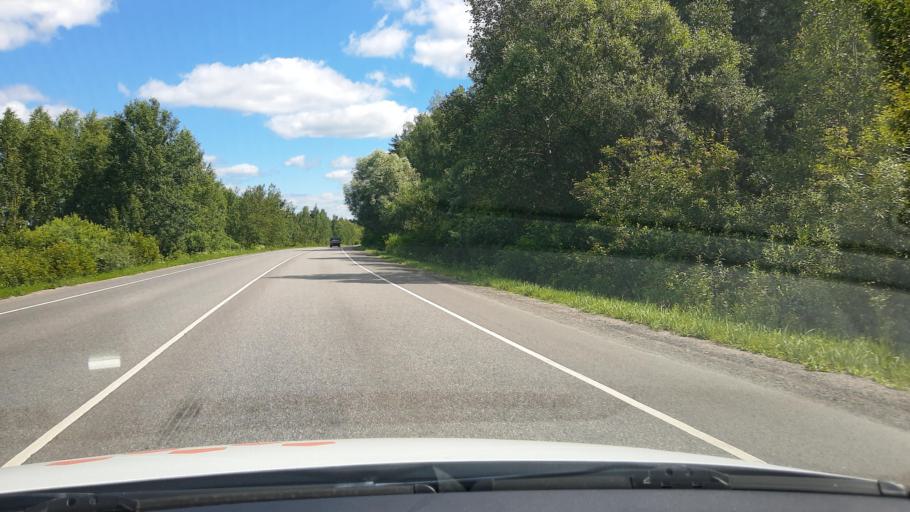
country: RU
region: Moskovskaya
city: Noginsk
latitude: 55.8632
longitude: 38.4134
